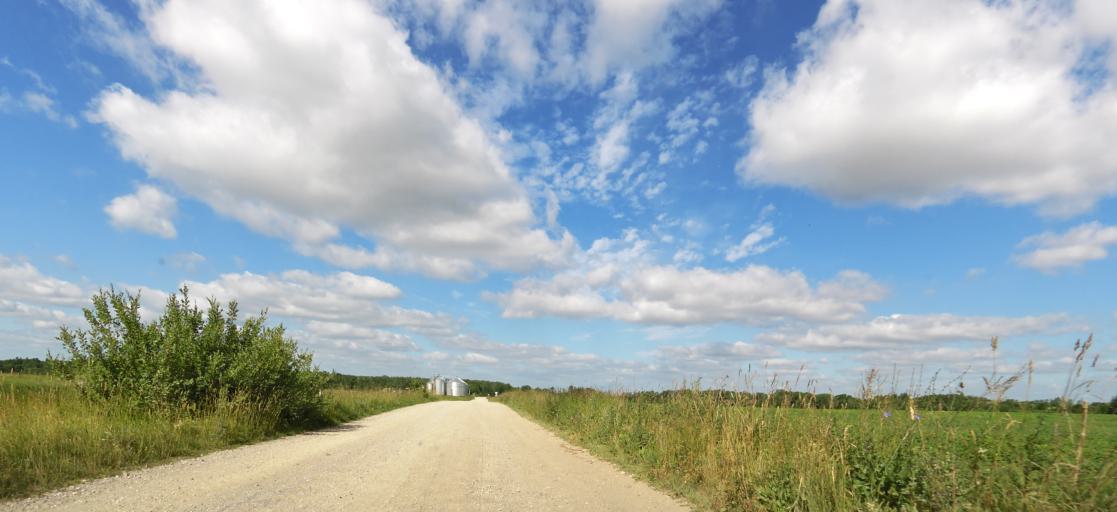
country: LT
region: Panevezys
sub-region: Birzai
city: Birzai
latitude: 56.1802
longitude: 24.7595
